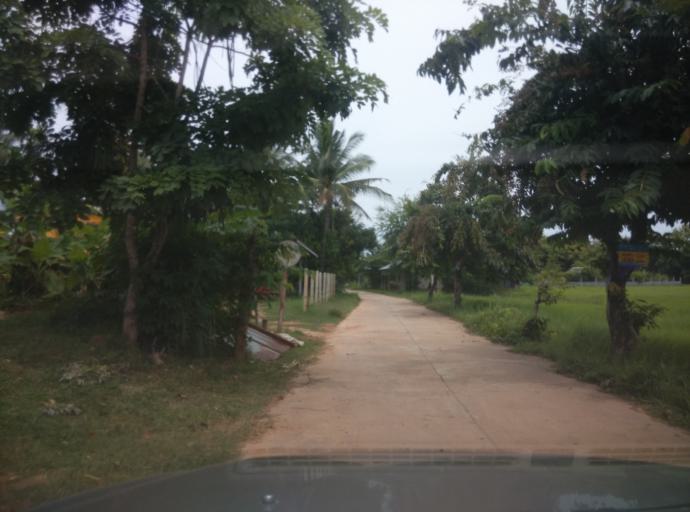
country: TH
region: Sisaket
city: Huai Thap Than
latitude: 15.0473
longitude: 104.0817
